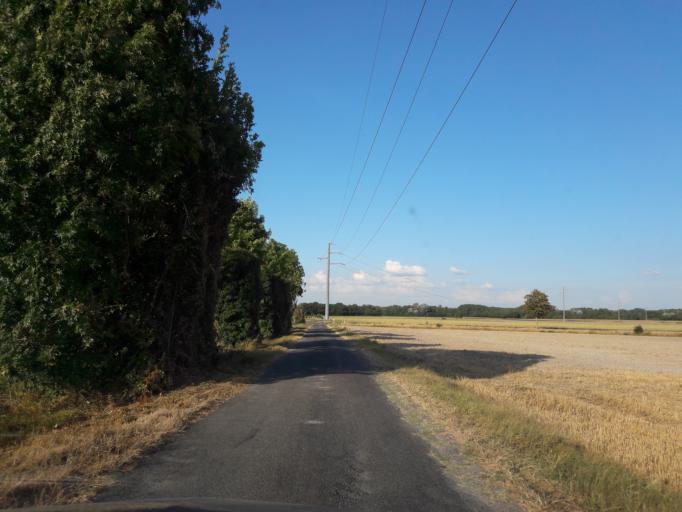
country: FR
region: Poitou-Charentes
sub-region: Departement de la Charente-Maritime
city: Les Gonds
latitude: 45.6677
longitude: -0.6004
